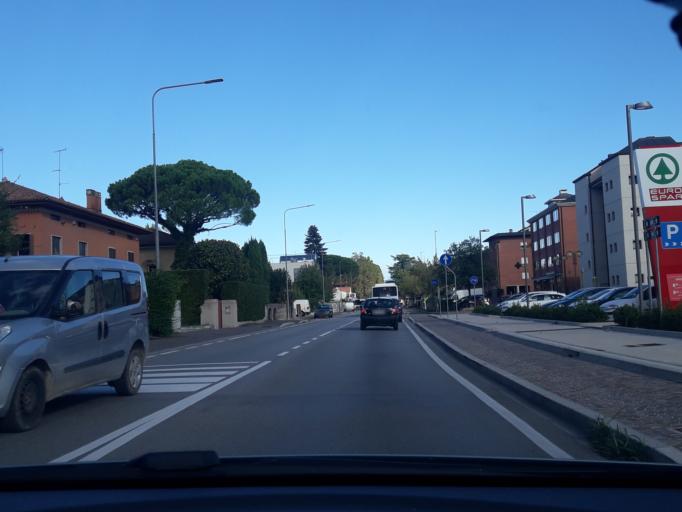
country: IT
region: Friuli Venezia Giulia
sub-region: Provincia di Udine
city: Colugna
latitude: 46.0792
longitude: 13.2187
